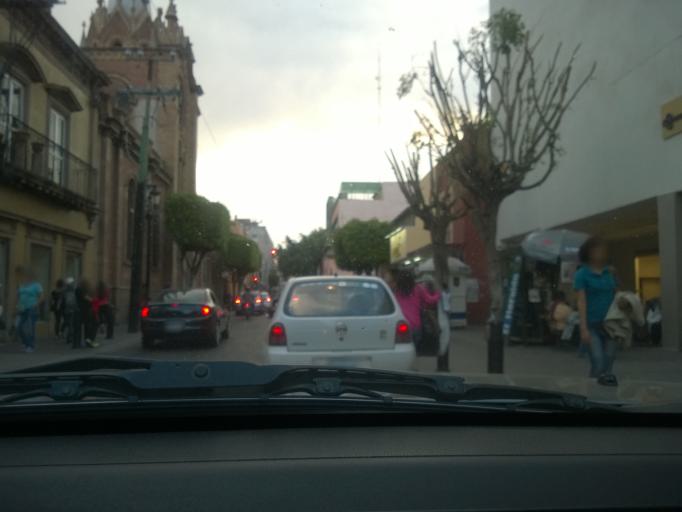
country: MX
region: Guanajuato
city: Leon
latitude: 21.1241
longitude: -101.6829
